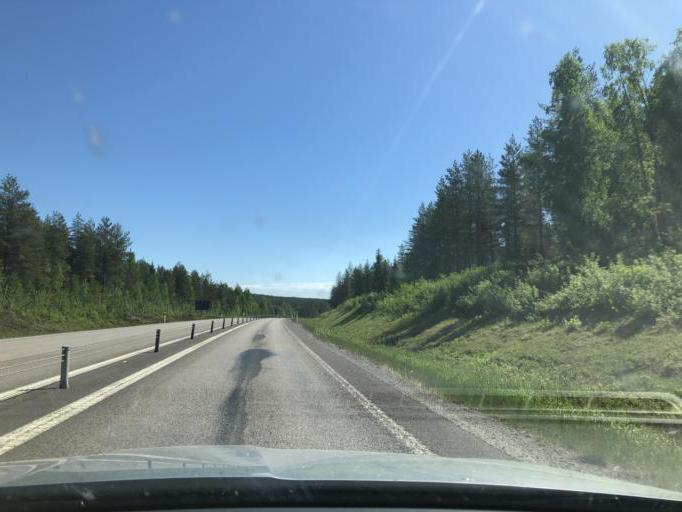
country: SE
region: Norrbotten
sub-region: Kalix Kommun
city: Toere
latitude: 65.9172
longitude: 22.7659
